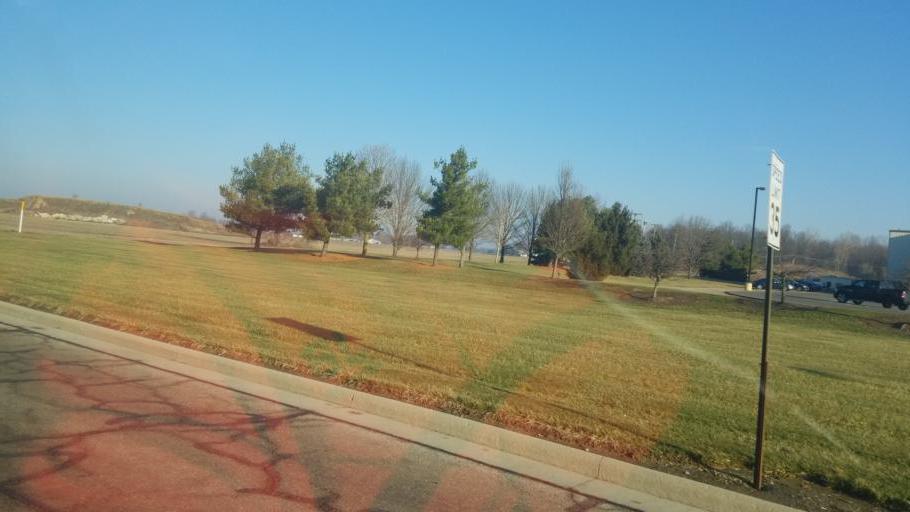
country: US
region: Ohio
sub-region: Crawford County
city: Bucyrus
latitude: 40.8311
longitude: -82.9637
